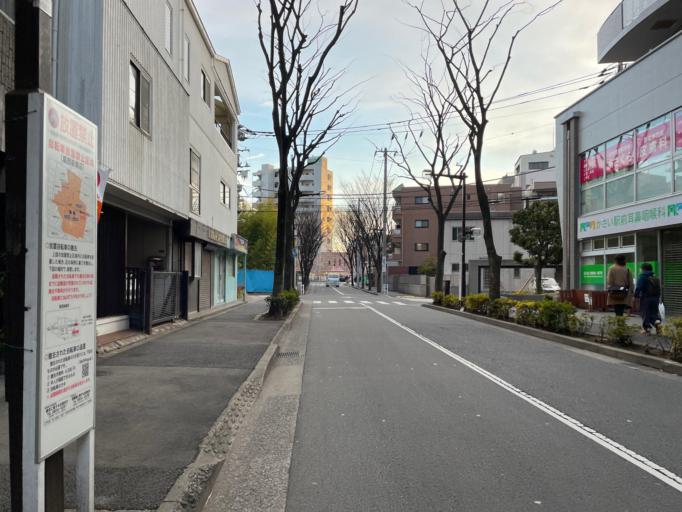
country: JP
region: Tokyo
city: Urayasu
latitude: 35.6615
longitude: 139.8719
